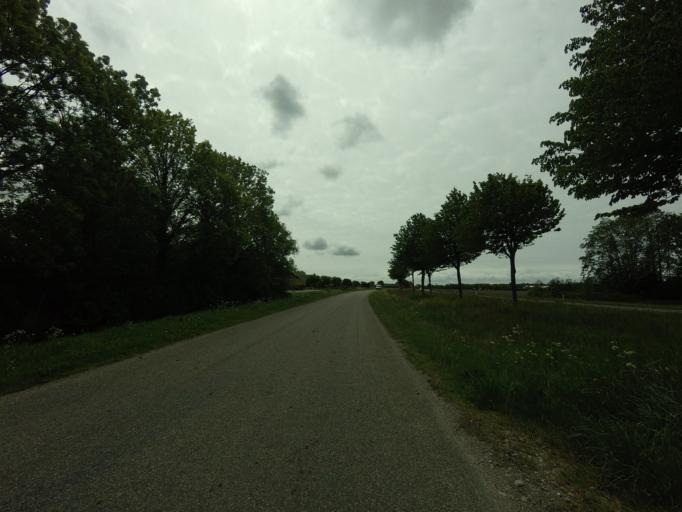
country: NL
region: Friesland
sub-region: Sudwest Fryslan
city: Koudum
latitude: 52.9173
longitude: 5.4630
